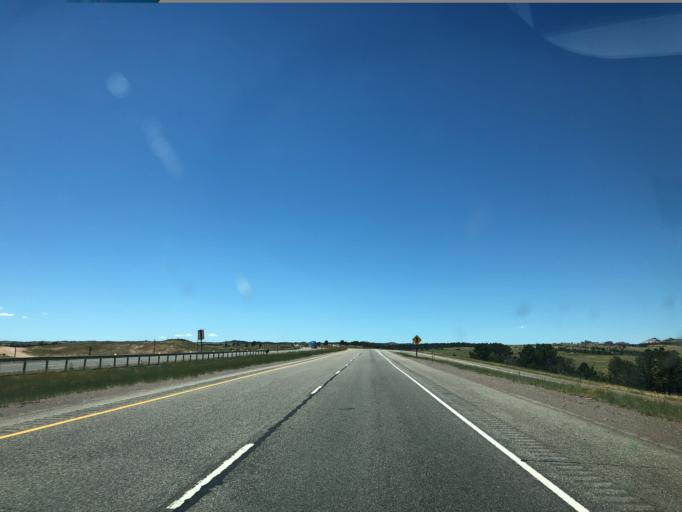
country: US
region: Wyoming
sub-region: Albany County
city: Laramie
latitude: 41.1250
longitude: -105.3053
